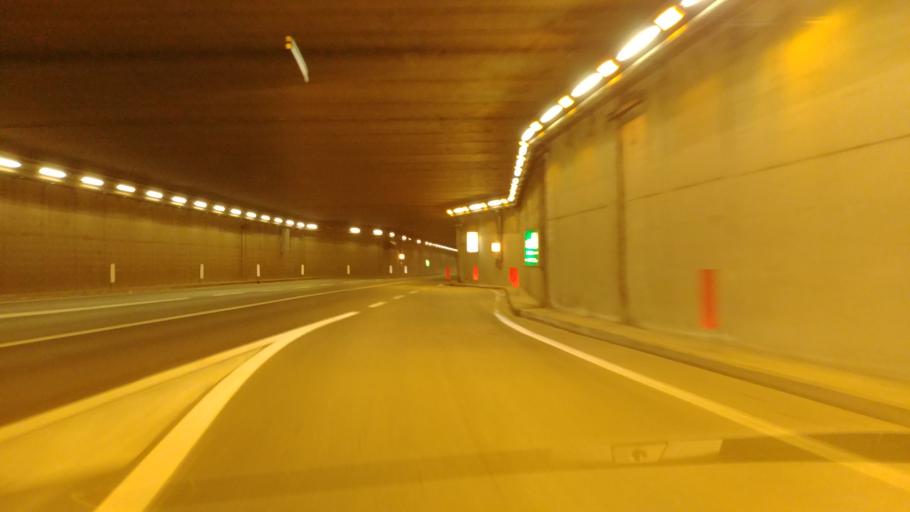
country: IT
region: Piedmont
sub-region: Provincia di Cuneo
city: Cuneo
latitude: 44.3758
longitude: 7.5376
